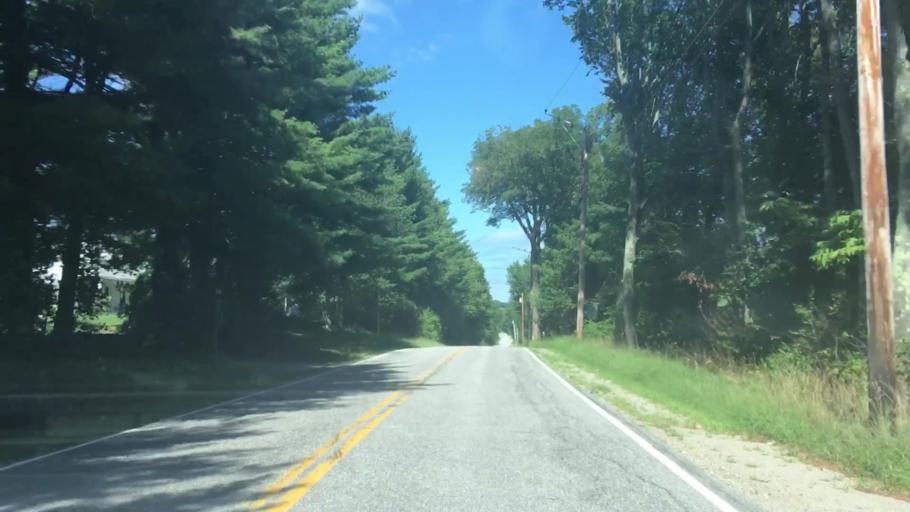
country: US
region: Maine
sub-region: Kennebec County
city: Monmouth
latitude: 44.1792
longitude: -69.9400
